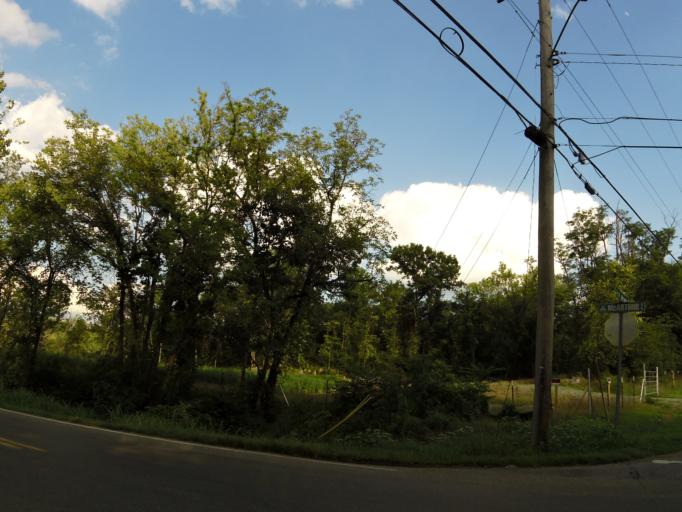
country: US
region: Tennessee
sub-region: Blount County
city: Alcoa
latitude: 35.7882
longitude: -83.9628
